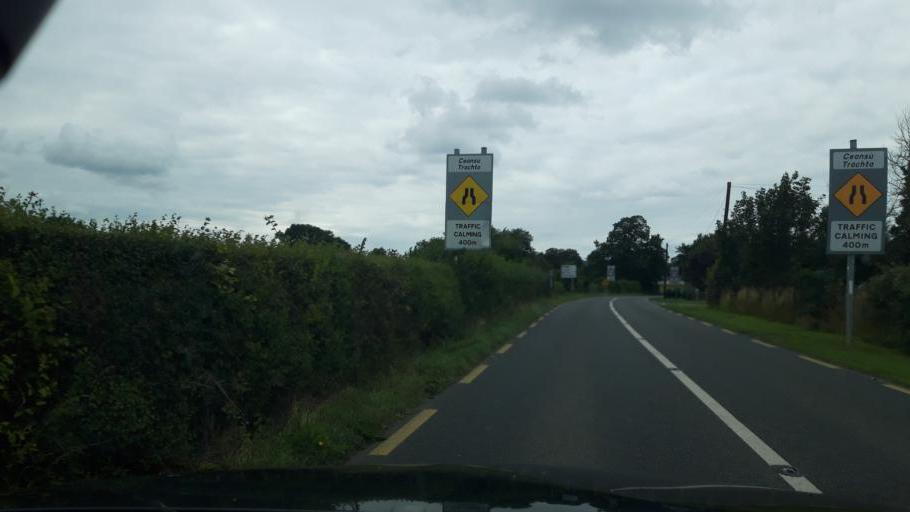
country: IE
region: Leinster
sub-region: Kilkenny
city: Thomastown
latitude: 52.6246
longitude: -7.0712
